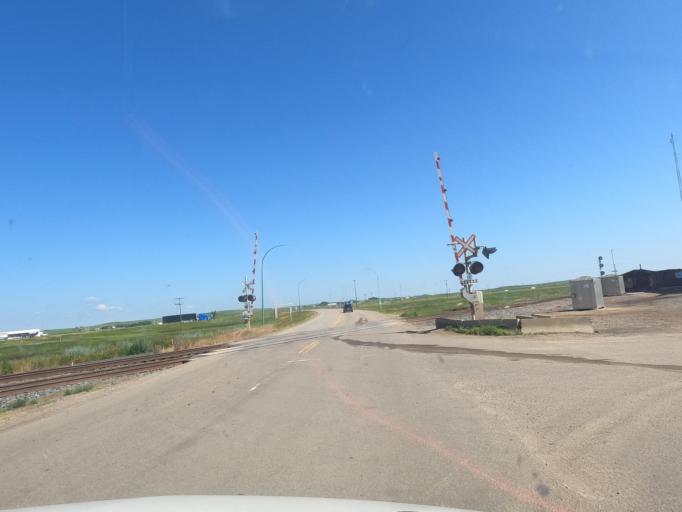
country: CA
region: Saskatchewan
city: Shaunavon
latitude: 50.0993
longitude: -108.4832
